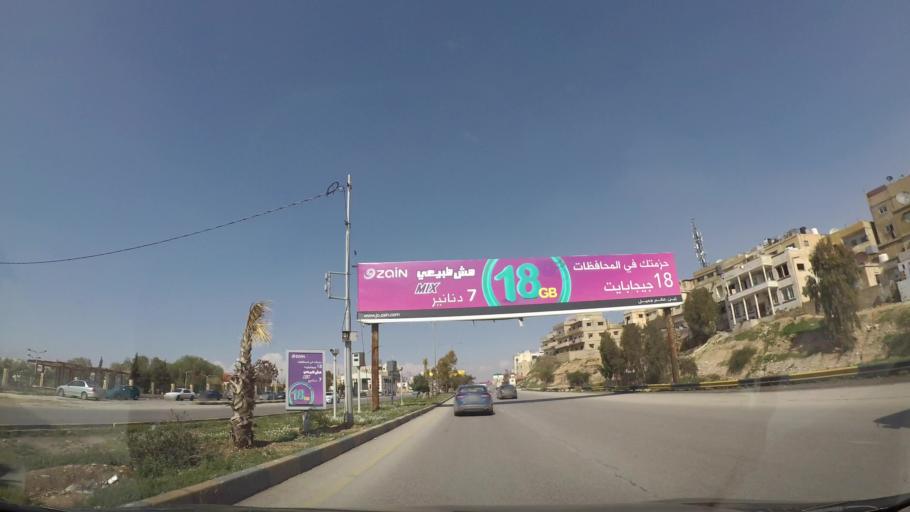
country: JO
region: Zarqa
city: Zarqa
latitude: 32.0301
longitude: 36.0887
